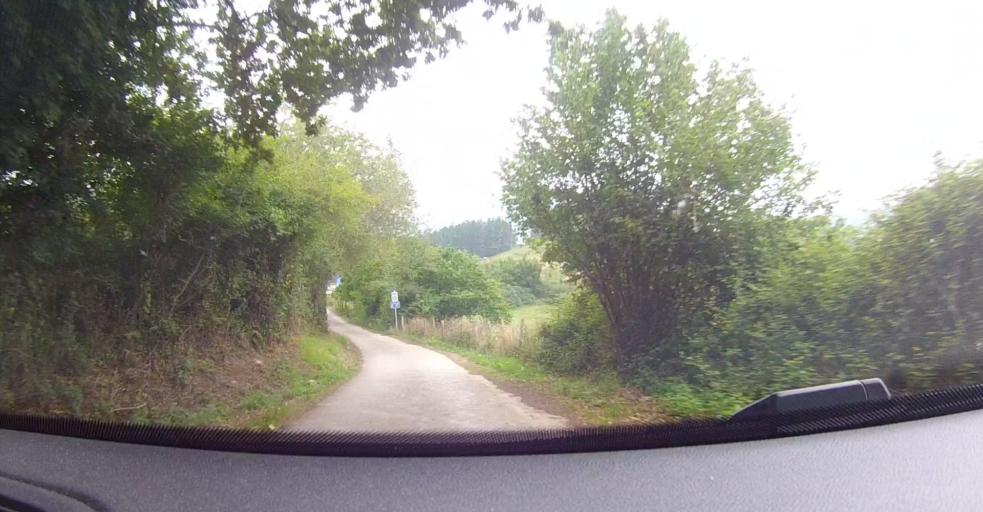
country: ES
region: Basque Country
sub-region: Bizkaia
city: Sopuerta
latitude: 43.2580
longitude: -3.1356
